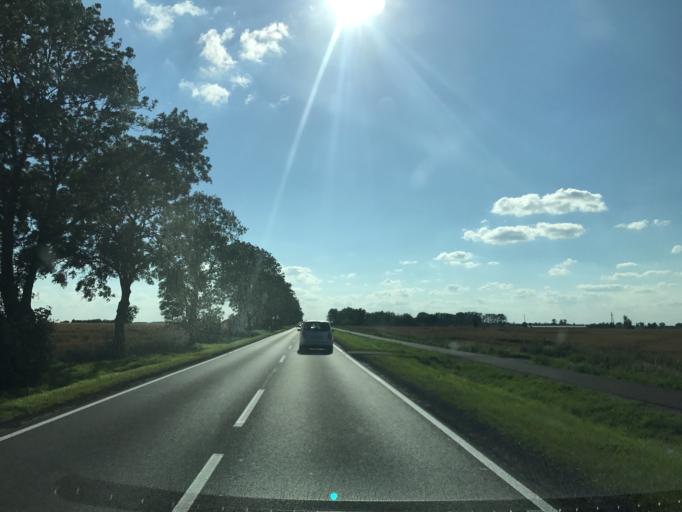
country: PL
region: Kujawsko-Pomorskie
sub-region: Powiat wloclawski
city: Brzesc Kujawski
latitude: 52.6165
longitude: 18.9381
